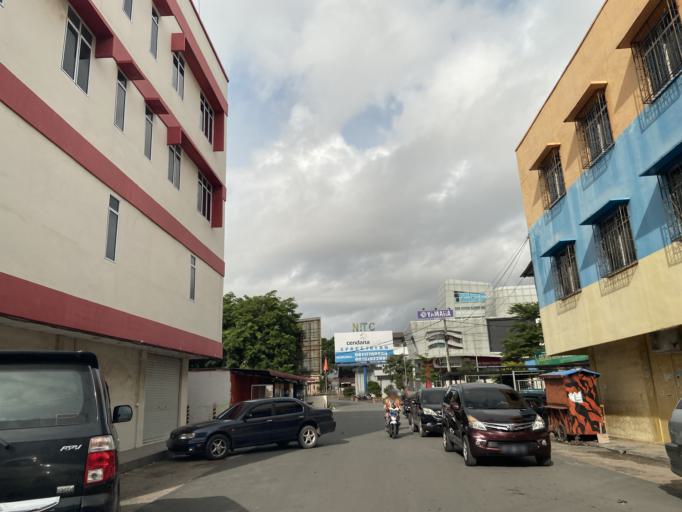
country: SG
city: Singapore
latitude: 1.1433
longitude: 104.0110
